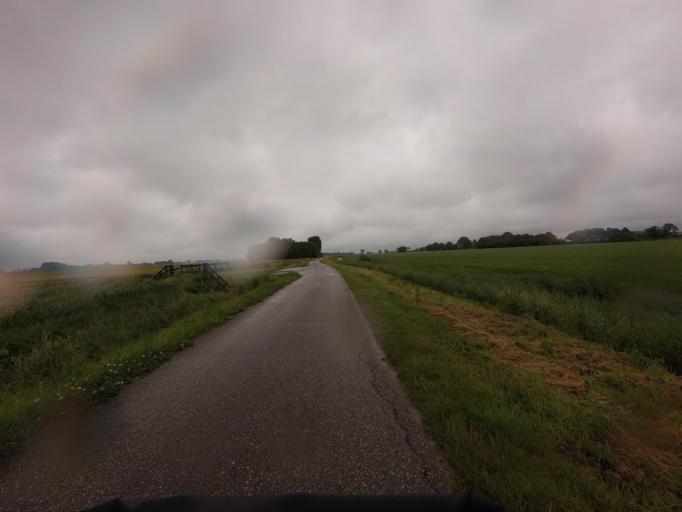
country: NL
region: North Holland
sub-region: Gemeente Opmeer
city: Opmeer
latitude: 52.7453
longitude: 4.9368
